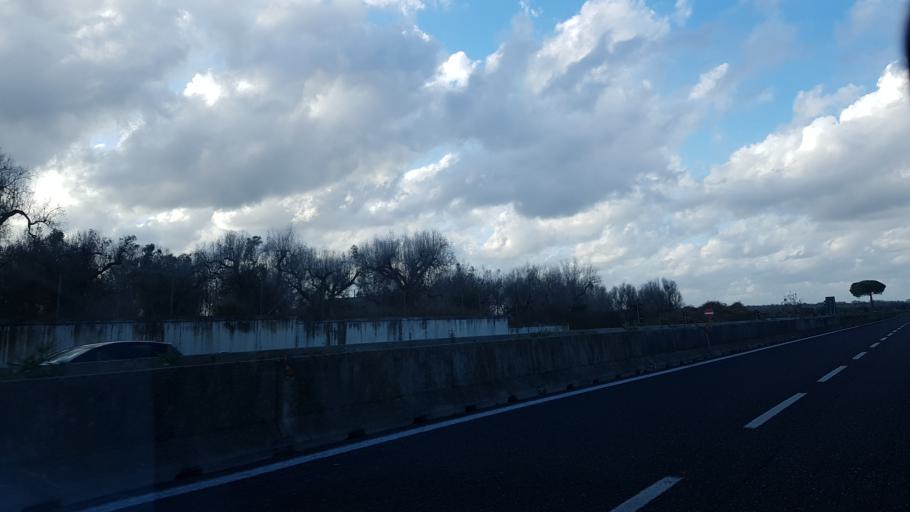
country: IT
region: Apulia
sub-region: Provincia di Brindisi
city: Torchiarolo
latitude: 40.4631
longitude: 18.0577
